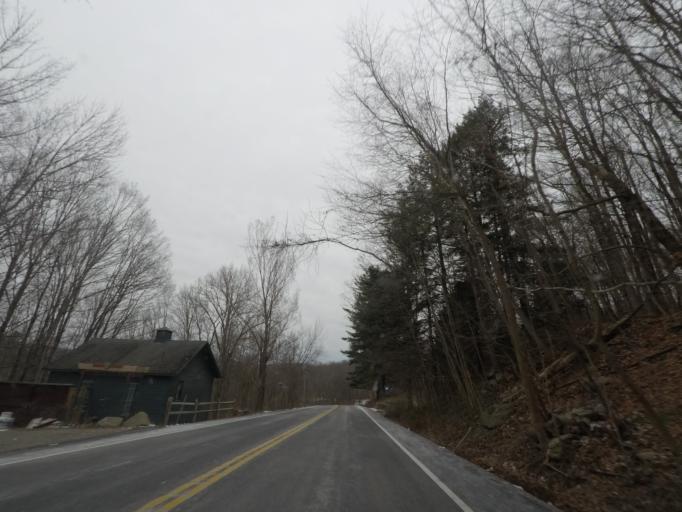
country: US
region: New York
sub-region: Rensselaer County
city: Hoosick Falls
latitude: 42.7582
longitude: -73.3649
